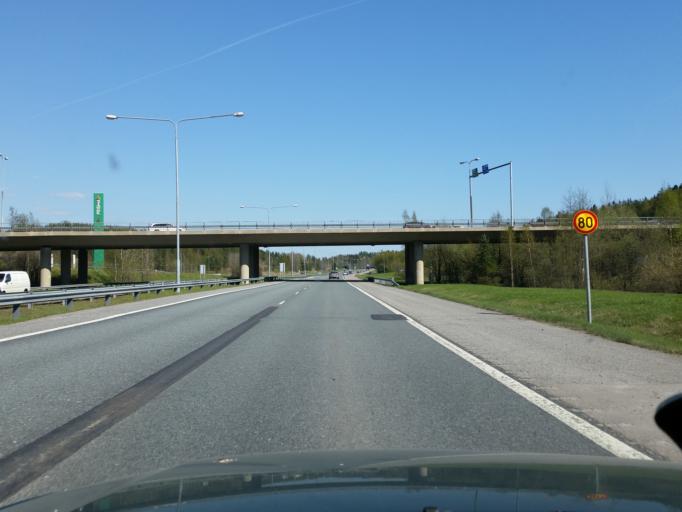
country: FI
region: Uusimaa
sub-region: Helsinki
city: Kirkkonummi
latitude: 60.1165
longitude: 24.4420
